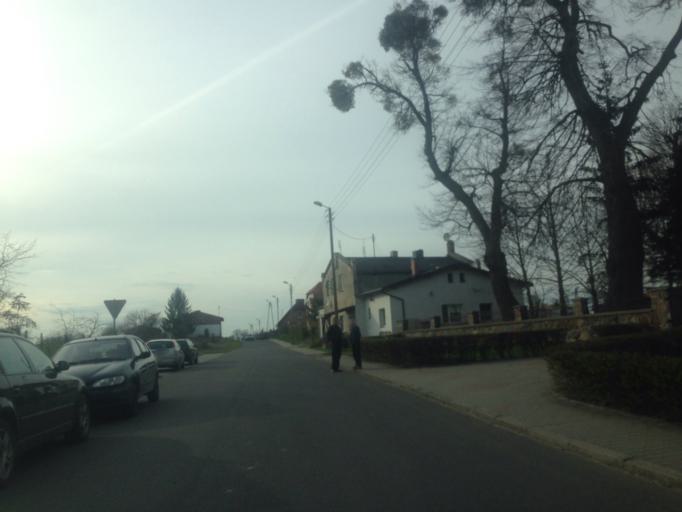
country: PL
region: Kujawsko-Pomorskie
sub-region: Powiat grudziadzki
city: Swiecie nad Osa
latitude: 53.4655
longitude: 19.1628
